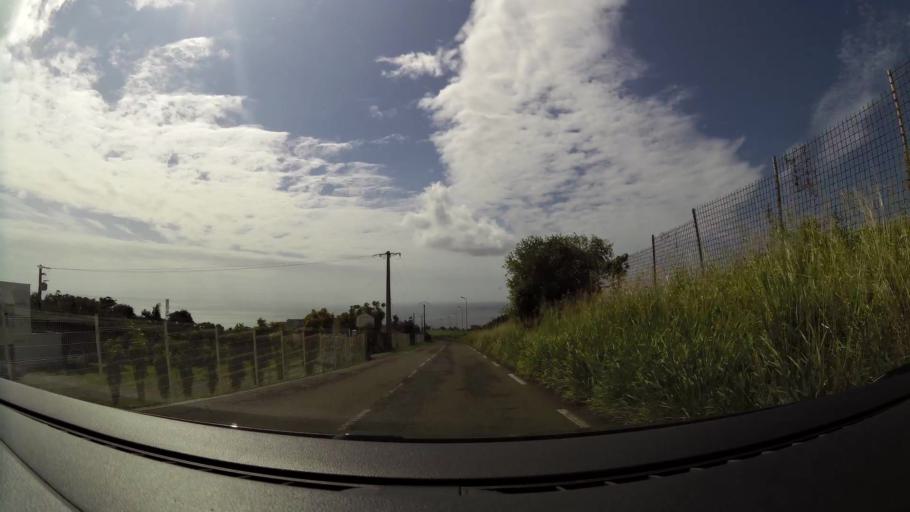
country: GP
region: Guadeloupe
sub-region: Guadeloupe
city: Basse-Terre
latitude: 16.0092
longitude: -61.7284
